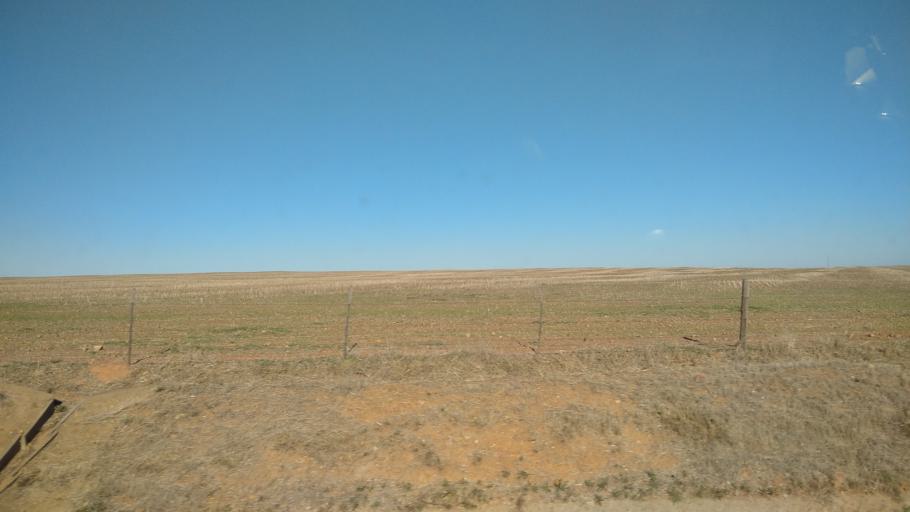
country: ZA
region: Western Cape
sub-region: West Coast District Municipality
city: Malmesbury
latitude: -33.3515
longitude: 18.6419
